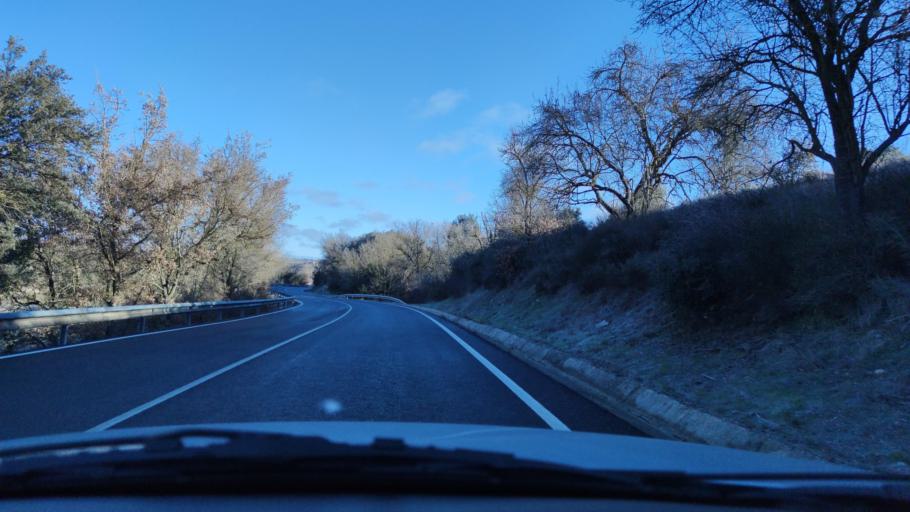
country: ES
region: Catalonia
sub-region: Provincia de Lleida
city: Cervera
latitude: 41.6867
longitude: 1.3046
